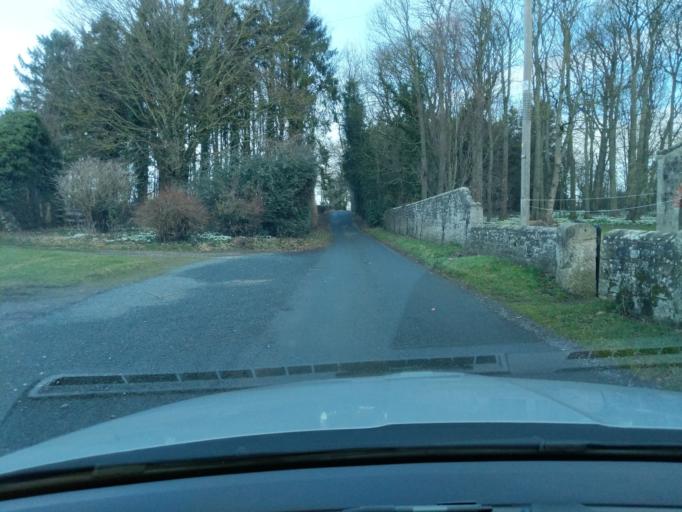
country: GB
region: England
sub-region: North Yorkshire
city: Catterick
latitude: 54.3776
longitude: -1.6715
